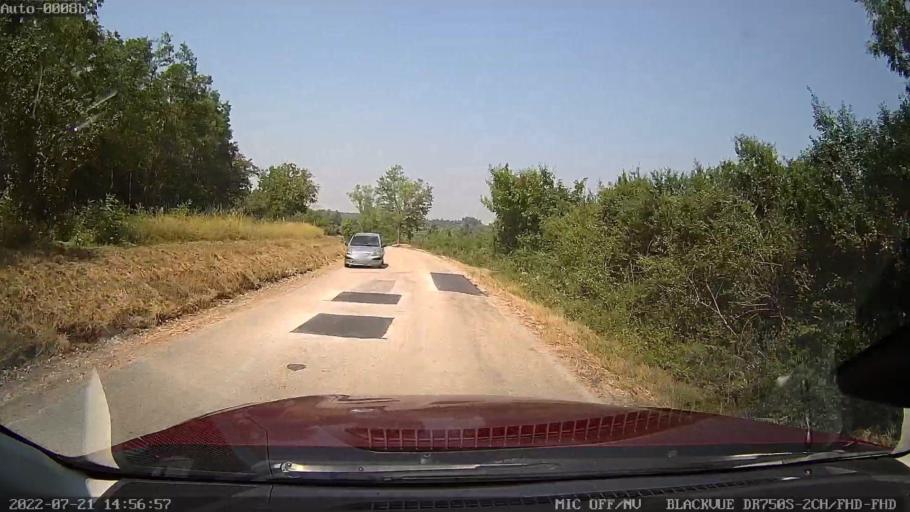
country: HR
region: Istarska
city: Pazin
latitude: 45.2049
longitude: 13.9509
